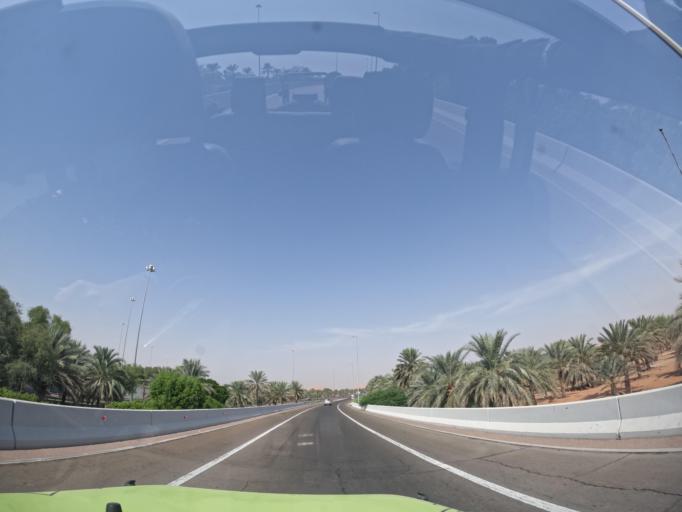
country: AE
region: Abu Dhabi
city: Al Ain
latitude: 24.2004
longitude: 55.5851
